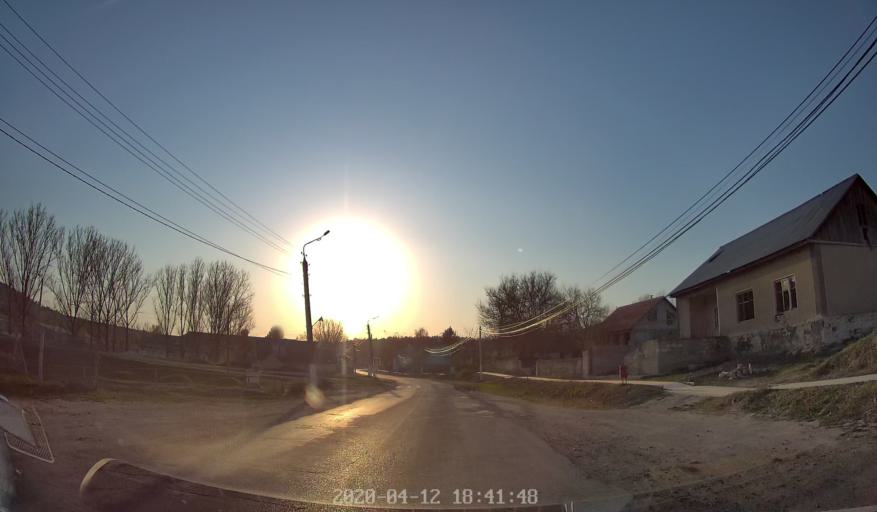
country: MD
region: Chisinau
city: Ciorescu
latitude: 47.1356
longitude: 28.9462
